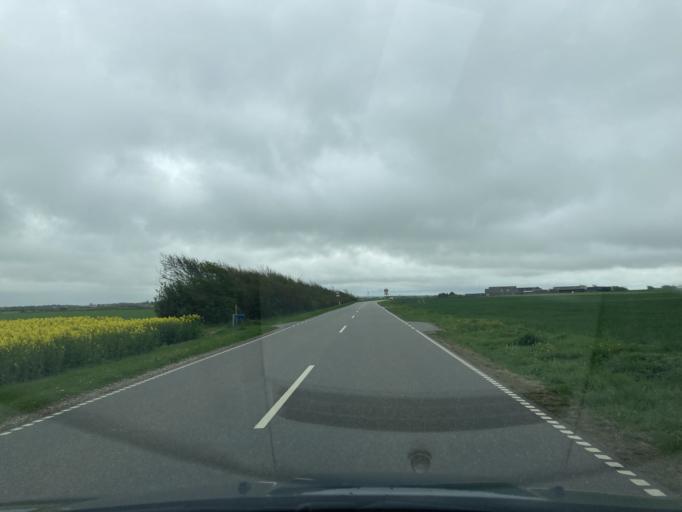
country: DK
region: North Denmark
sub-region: Thisted Kommune
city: Hurup
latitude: 56.8321
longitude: 8.3600
